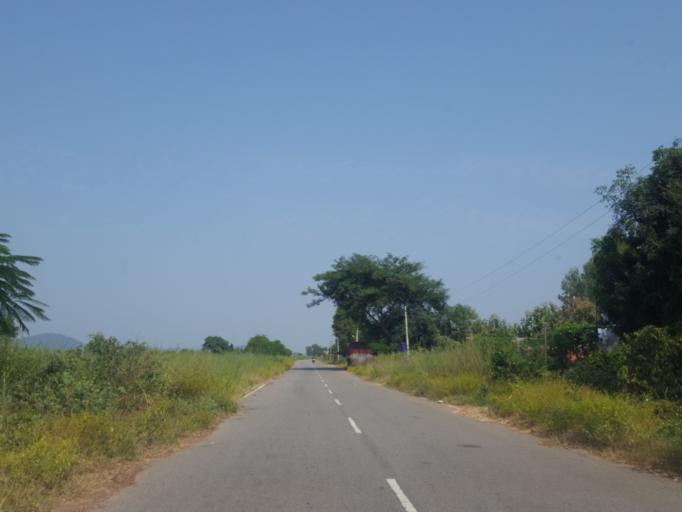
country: IN
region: Telangana
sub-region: Khammam
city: Yellandu
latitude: 17.6597
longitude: 80.2768
